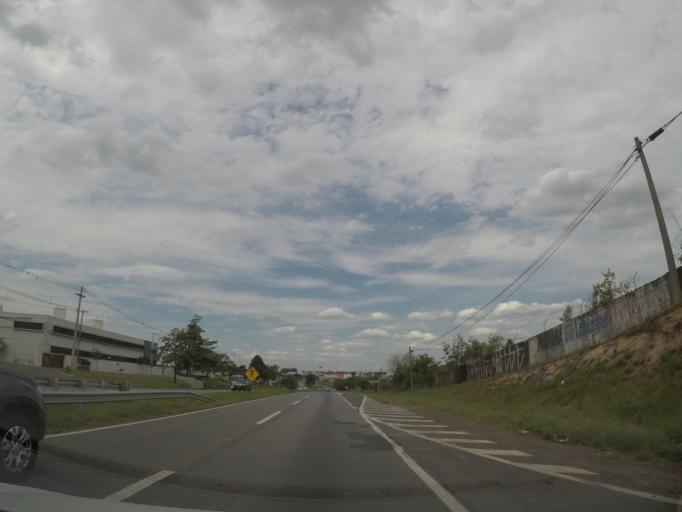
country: BR
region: Sao Paulo
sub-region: Sumare
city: Sumare
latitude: -22.8066
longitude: -47.2469
